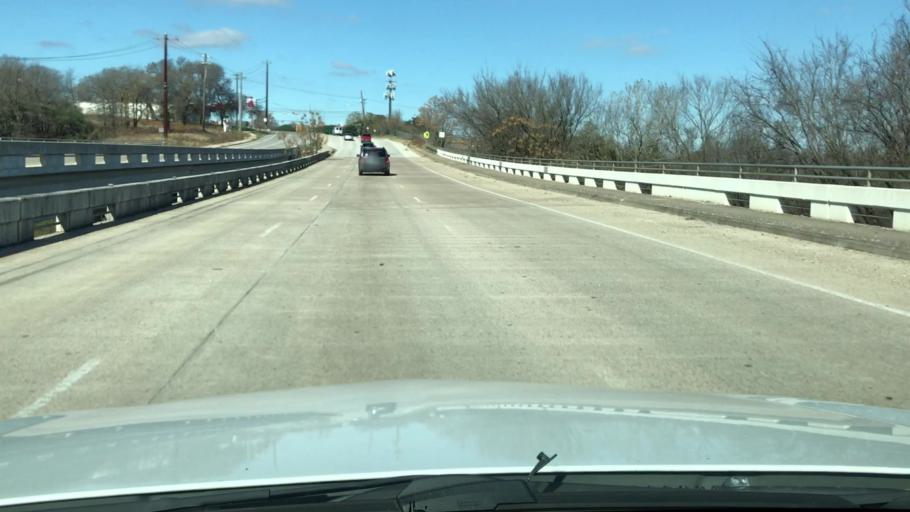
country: US
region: Texas
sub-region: Travis County
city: Onion Creek
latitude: 30.1778
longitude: -97.7449
